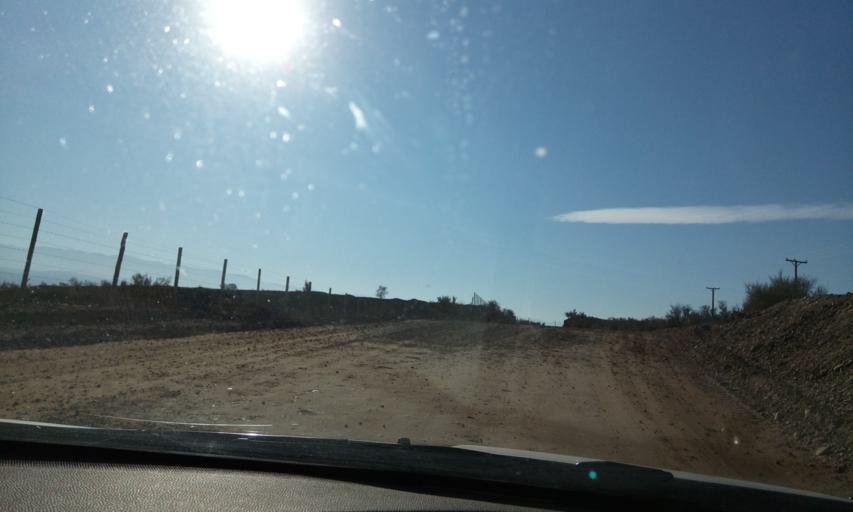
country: AR
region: San Juan
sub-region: Departamento de Rivadavia
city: Rivadavia
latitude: -31.4187
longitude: -68.6705
